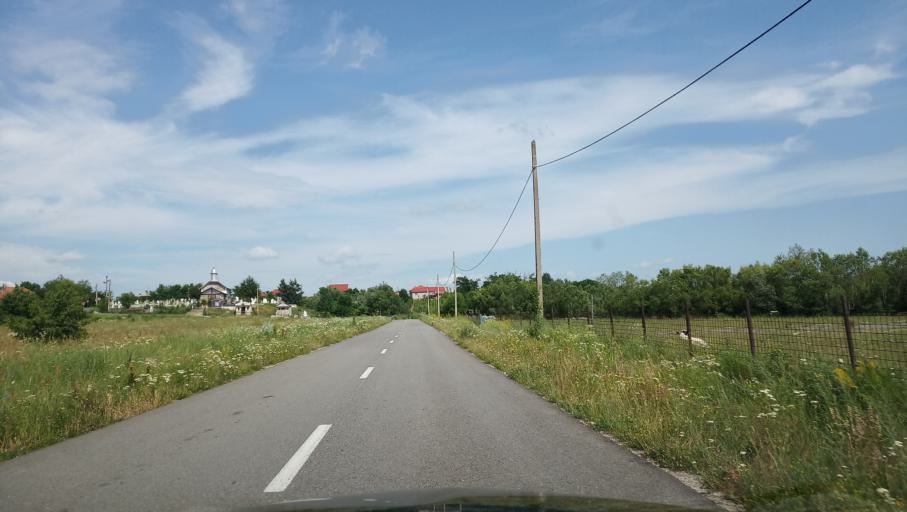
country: RO
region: Gorj
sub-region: Comuna Bumbesti-Jiu
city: Bumbesti-Jiu
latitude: 45.1306
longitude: 23.3817
